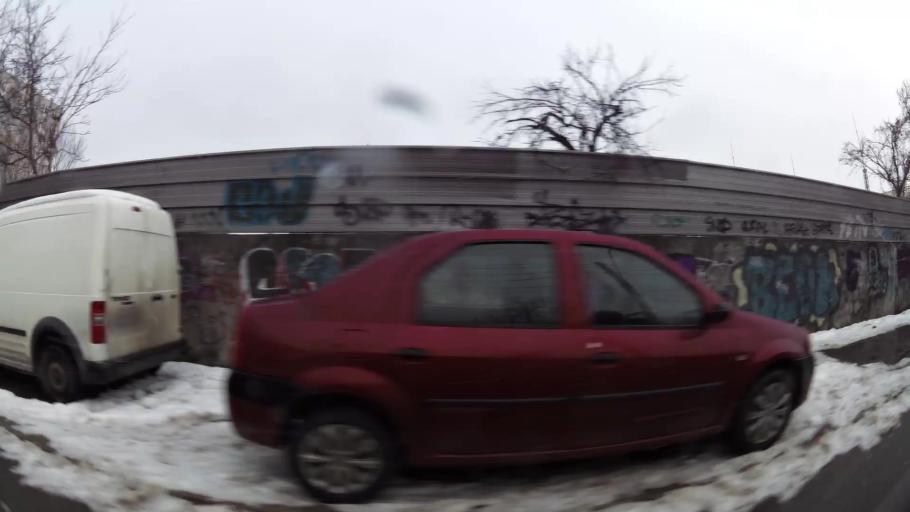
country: RO
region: Ilfov
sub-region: Comuna Mogosoaia
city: Mogosoaia
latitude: 44.4995
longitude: 26.0373
